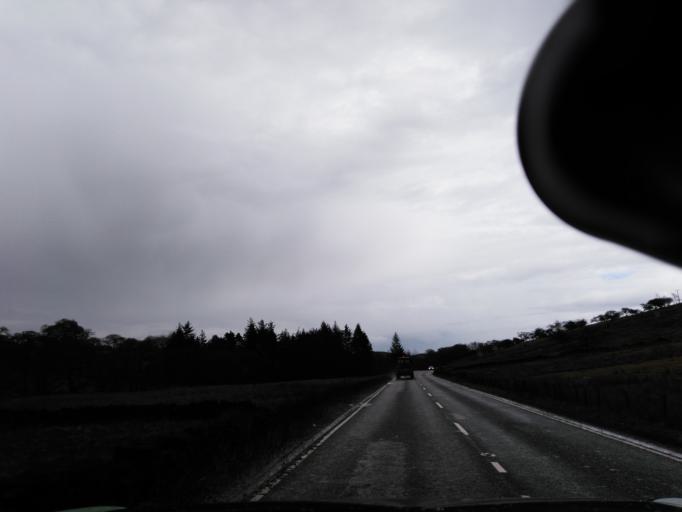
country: GB
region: England
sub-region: Bradford
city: Burley in Wharfedale
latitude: 53.9935
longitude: -1.7612
